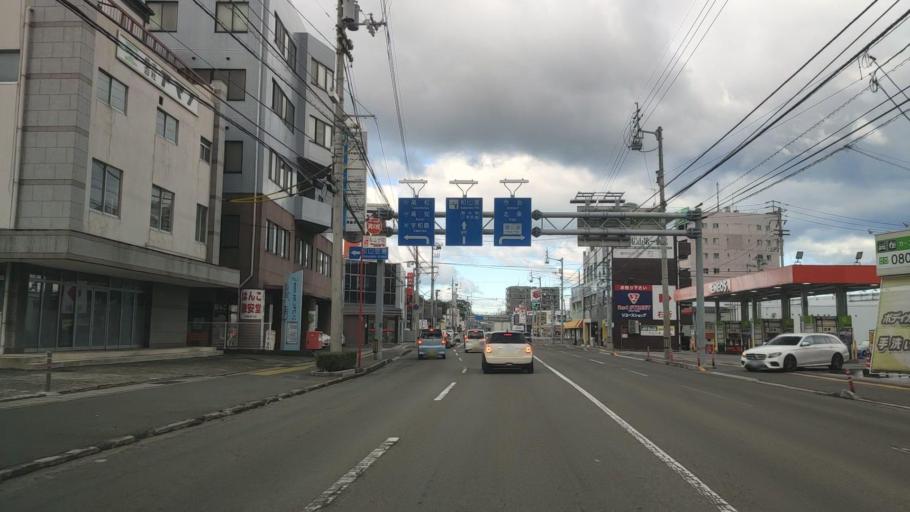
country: JP
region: Ehime
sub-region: Shikoku-chuo Shi
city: Matsuyama
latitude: 33.8548
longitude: 132.7492
